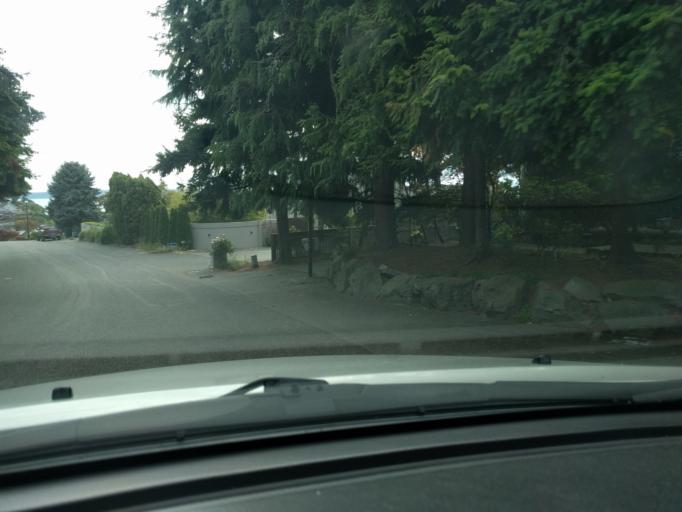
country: US
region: Washington
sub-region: King County
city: Shoreline
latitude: 47.7037
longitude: -122.3850
